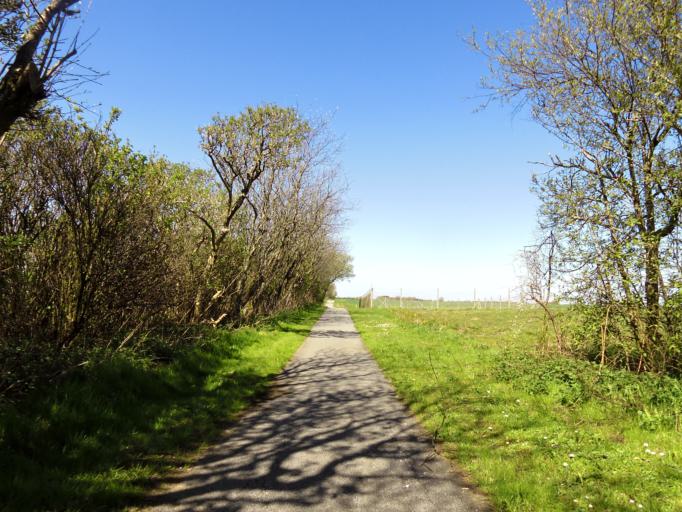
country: DK
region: Central Jutland
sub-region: Holstebro Kommune
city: Vinderup
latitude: 56.5949
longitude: 8.7904
